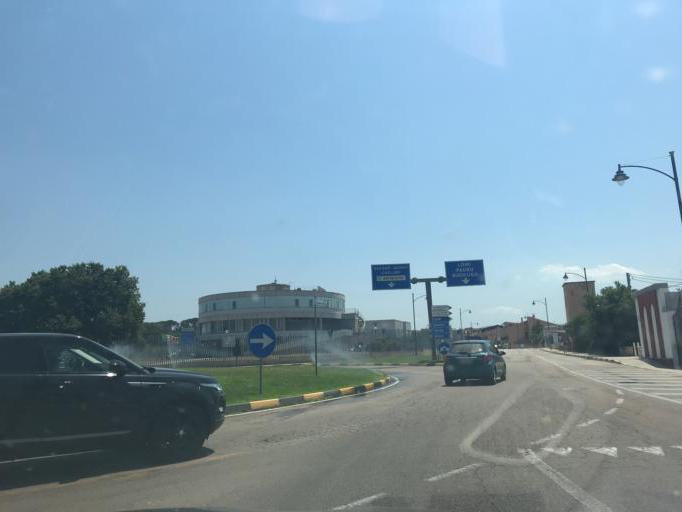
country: IT
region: Sardinia
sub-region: Provincia di Olbia-Tempio
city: Olbia
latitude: 40.9123
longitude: 9.5008
